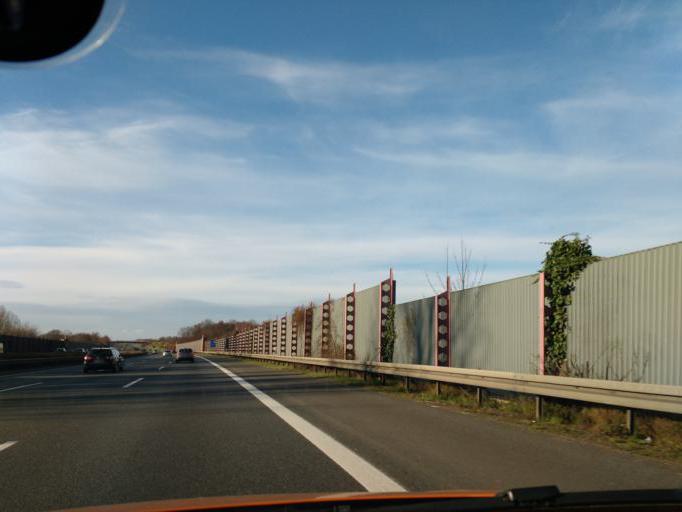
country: DE
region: Lower Saxony
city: Dollbergen
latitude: 52.3582
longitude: 10.1793
